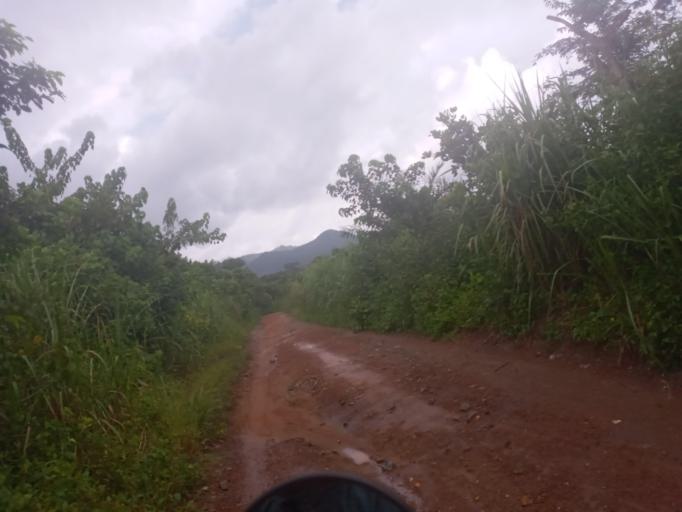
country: SL
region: Northern Province
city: Bumbuna
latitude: 8.9310
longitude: -11.7481
